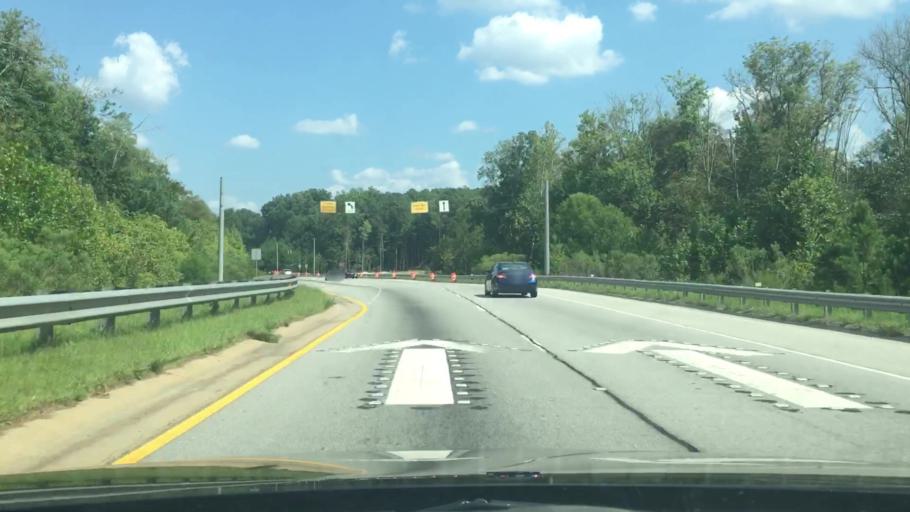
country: US
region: Georgia
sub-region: DeKalb County
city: Lithonia
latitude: 33.7025
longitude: -84.1336
